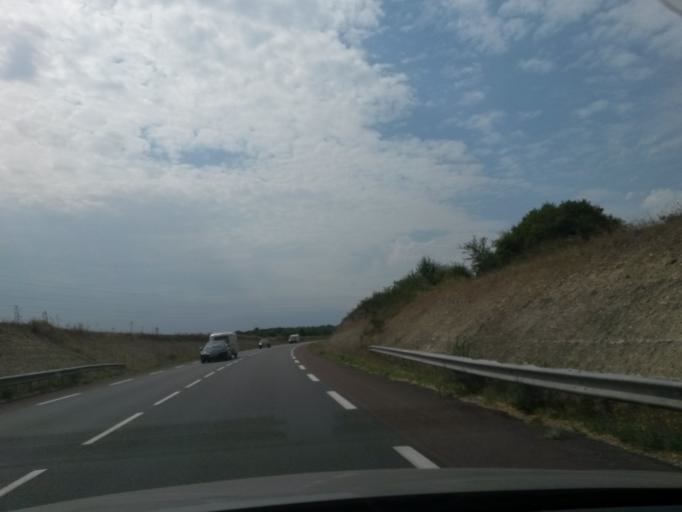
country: FR
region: Poitou-Charentes
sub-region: Departement de la Charente-Maritime
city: Saint-Xandre
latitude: 46.2045
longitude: -1.0900
